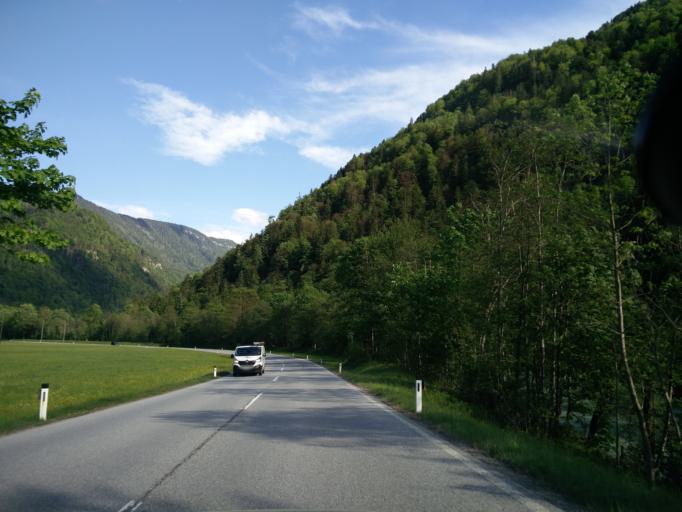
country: AT
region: Tyrol
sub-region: Politischer Bezirk Kitzbuhel
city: Kossen
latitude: 47.6471
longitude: 12.4387
